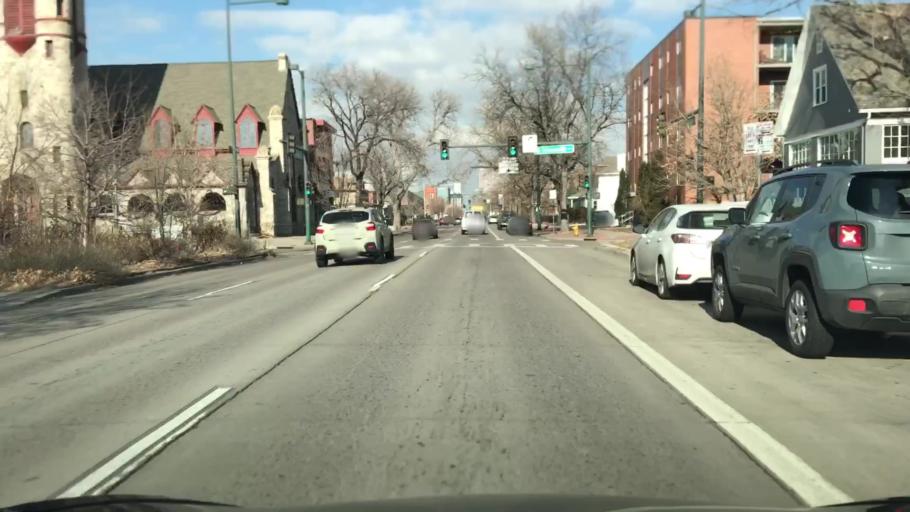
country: US
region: Colorado
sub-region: Denver County
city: Denver
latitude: 39.7162
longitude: -104.9863
